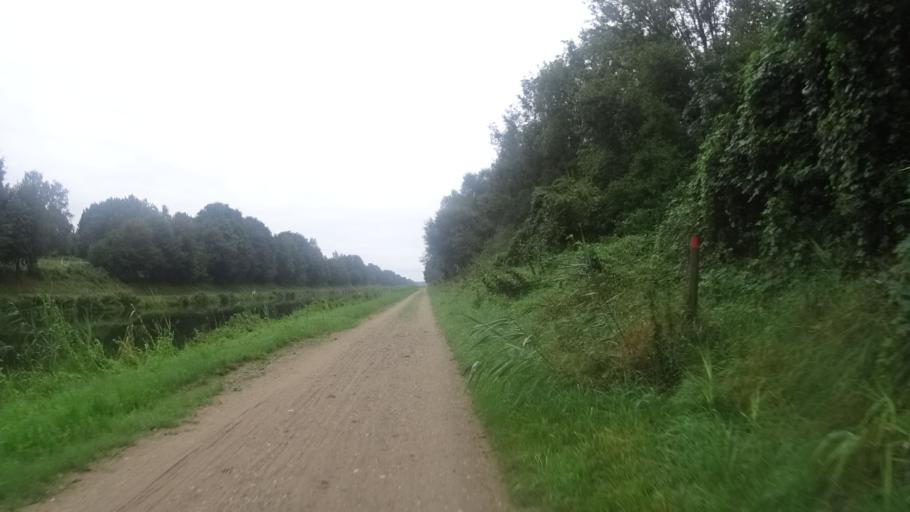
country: DE
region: Schleswig-Holstein
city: Grambek
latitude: 53.5738
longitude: 10.6750
